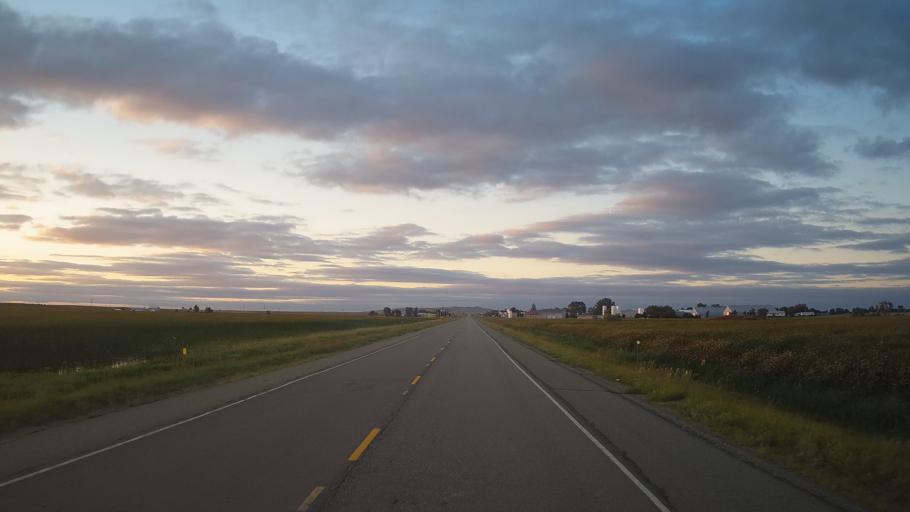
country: US
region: South Dakota
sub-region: Lyman County
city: Kennebec
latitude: 43.8697
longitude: -99.6061
